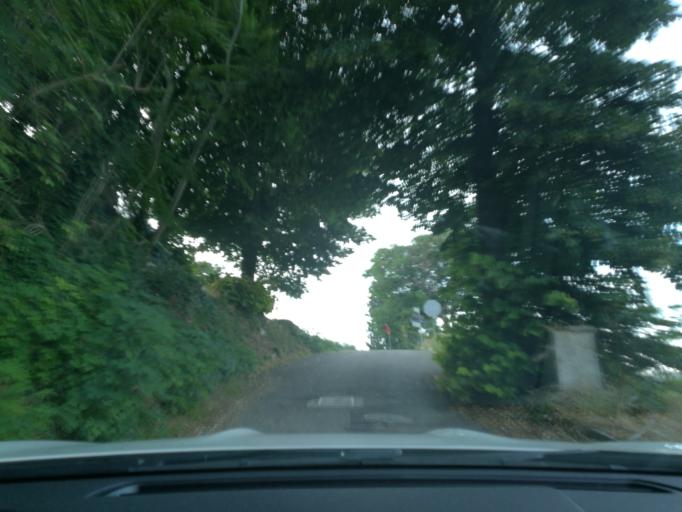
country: IT
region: Umbria
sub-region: Provincia di Terni
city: San Gemini
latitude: 42.6153
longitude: 12.5489
